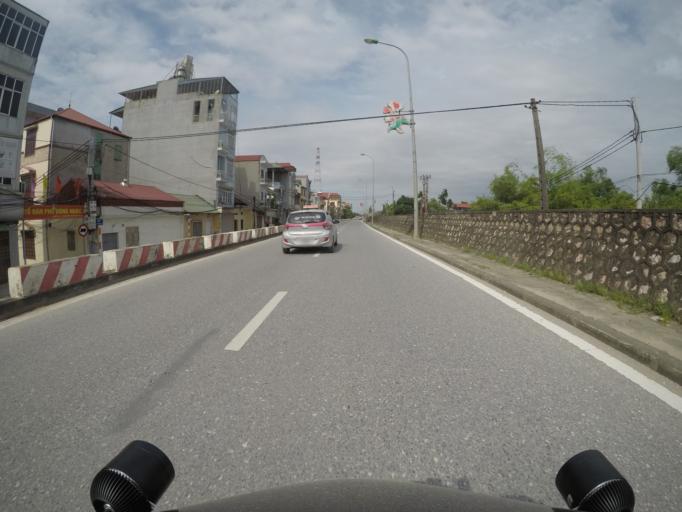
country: VN
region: Ha Noi
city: Tay Ho
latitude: 21.0923
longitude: 105.7819
